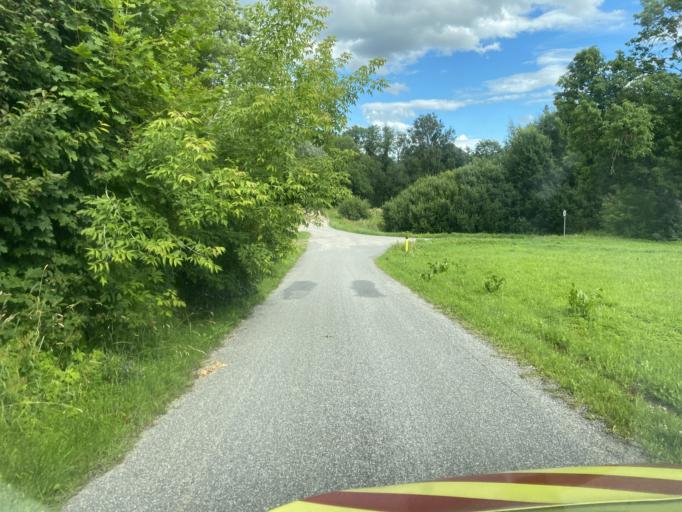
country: EE
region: Viljandimaa
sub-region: Viiratsi vald
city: Viiratsi
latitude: 58.3967
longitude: 25.8220
